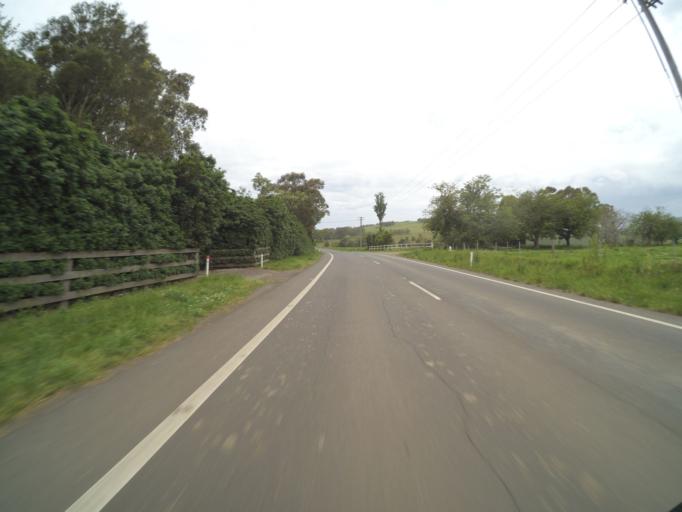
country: AU
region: New South Wales
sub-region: Kiama
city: Jamberoo
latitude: -34.6510
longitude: 150.7934
